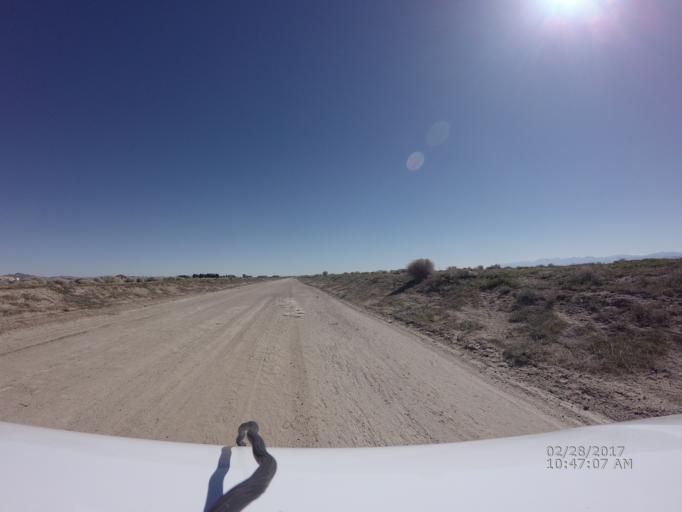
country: US
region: California
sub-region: Kern County
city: Rosamond
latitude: 34.8055
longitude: -118.2642
